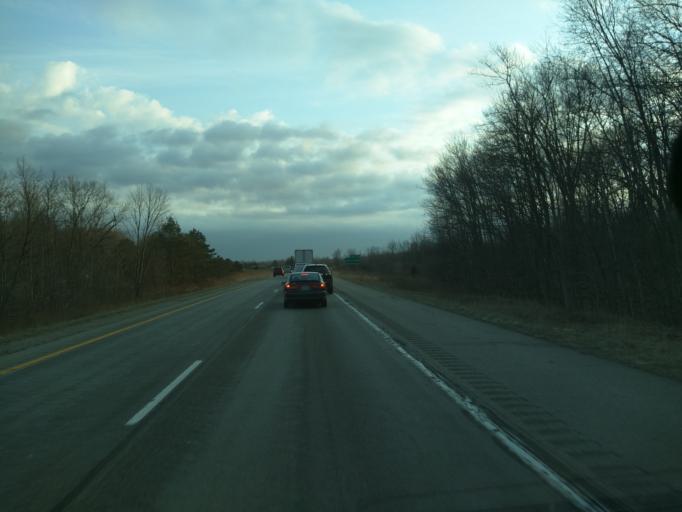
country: US
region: Michigan
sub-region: Ingham County
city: Holt
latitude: 42.6490
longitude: -84.4776
